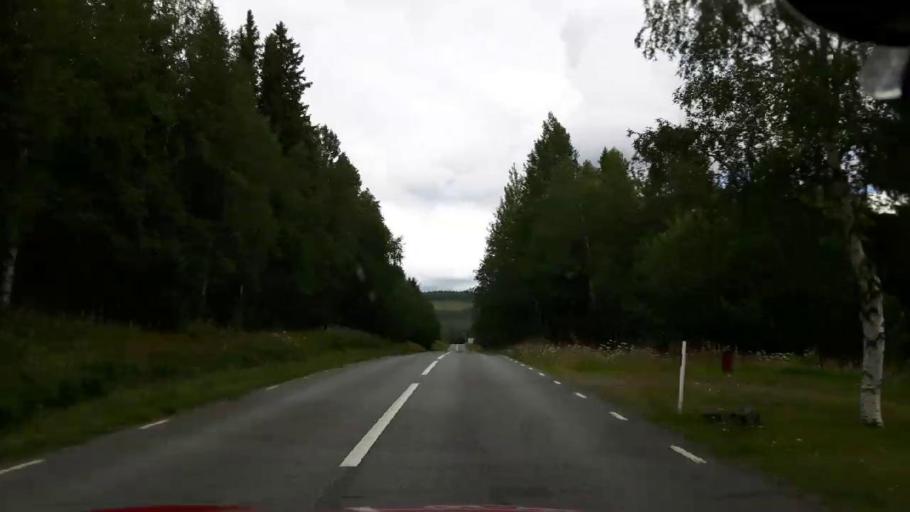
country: NO
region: Nord-Trondelag
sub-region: Lierne
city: Sandvika
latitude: 64.3925
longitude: 14.4790
